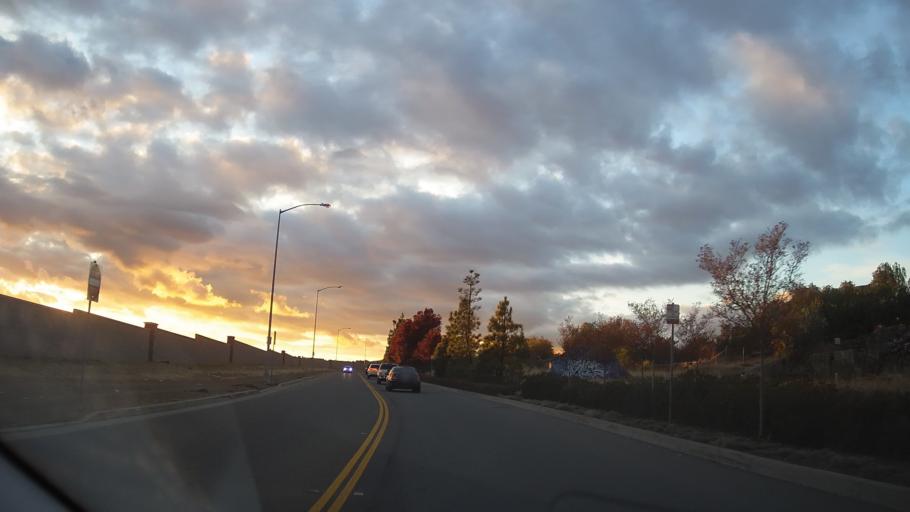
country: US
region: California
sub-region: Solano County
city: Fairfield
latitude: 38.2860
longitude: -121.9987
